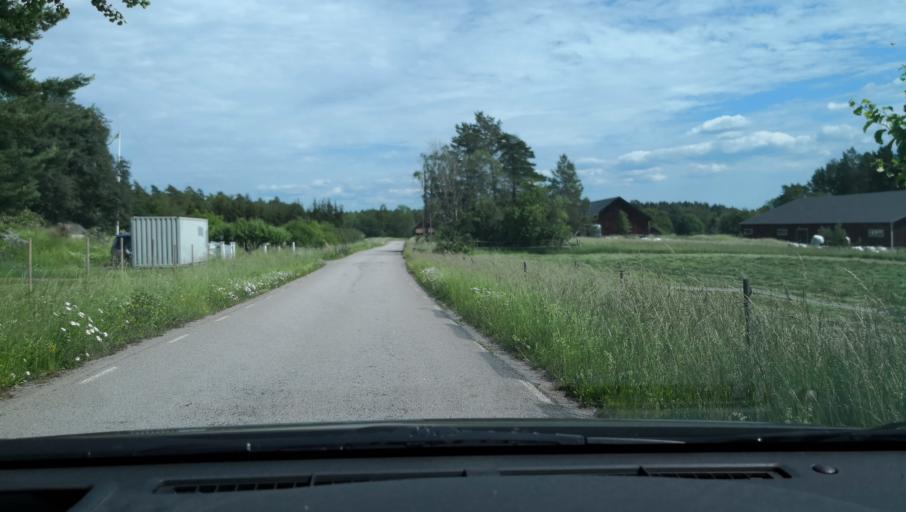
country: SE
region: Uppsala
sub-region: Uppsala Kommun
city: Alsike
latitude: 59.7035
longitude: 17.7002
